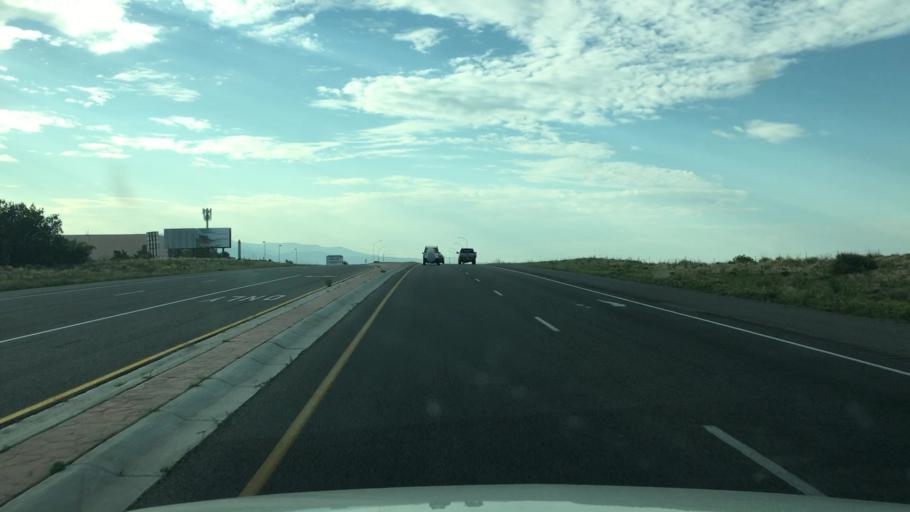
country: US
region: New Mexico
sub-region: Santa Fe County
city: El Valle de Arroyo Seco
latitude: 35.9803
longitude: -106.0477
